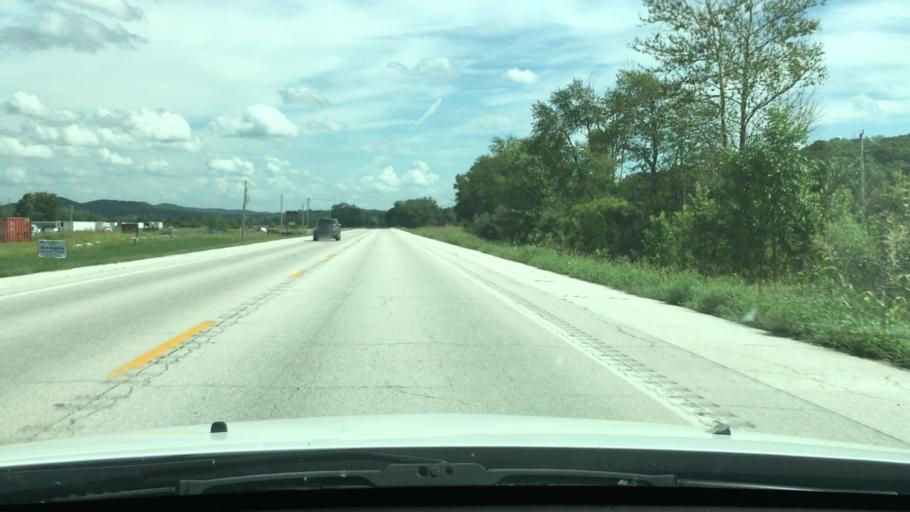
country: US
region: Missouri
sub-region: Pike County
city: Bowling Green
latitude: 39.3823
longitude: -91.1330
